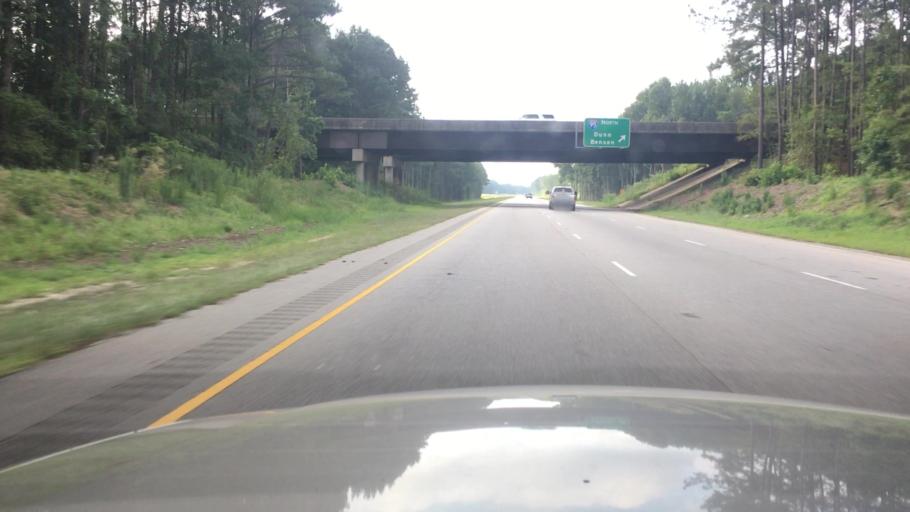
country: US
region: North Carolina
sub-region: Cumberland County
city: Fayetteville
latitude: 34.9769
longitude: -78.8572
